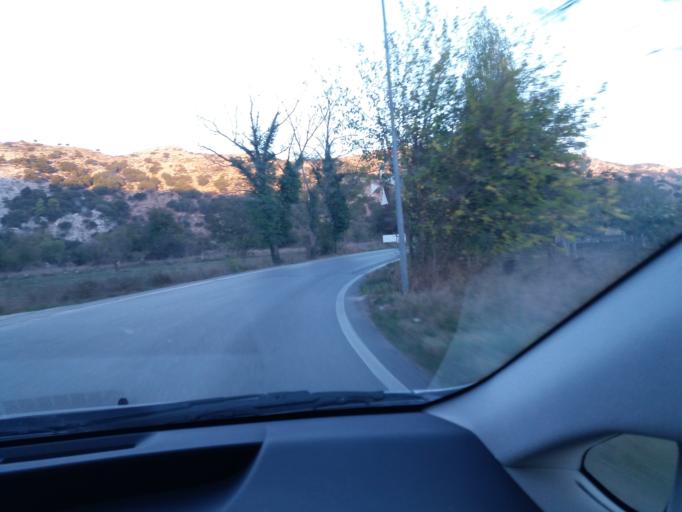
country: GR
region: Crete
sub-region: Nomos Irakleiou
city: Mokhos
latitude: 35.2038
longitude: 25.4747
